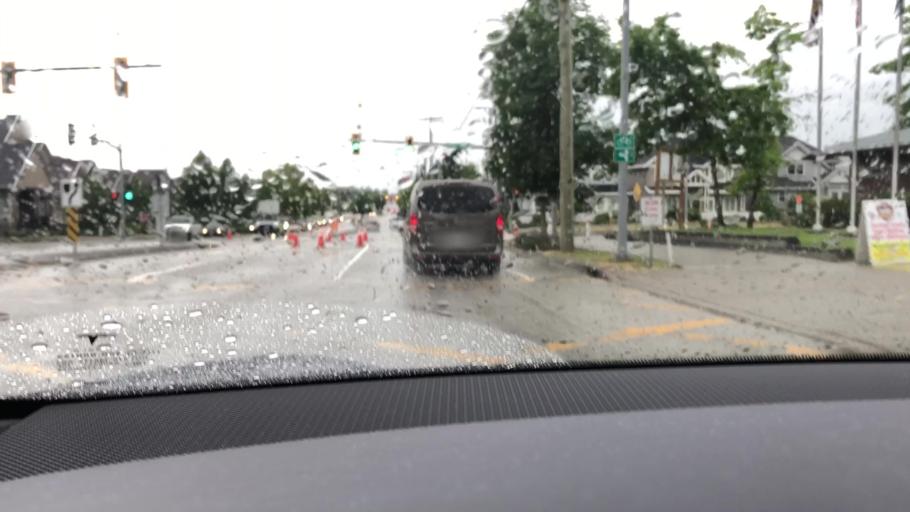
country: CA
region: British Columbia
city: Langley
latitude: 49.1334
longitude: -122.6608
